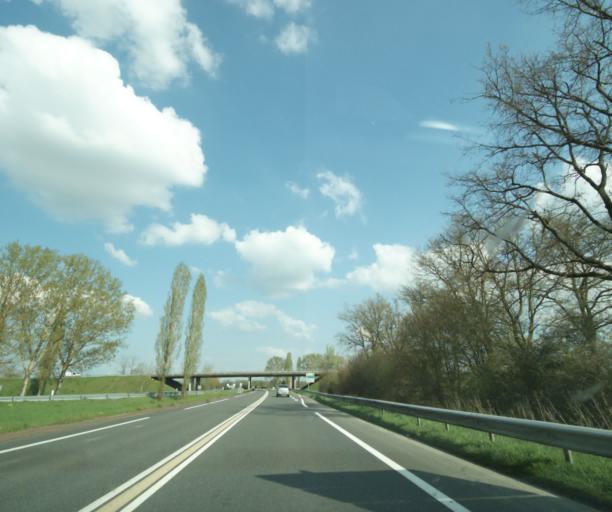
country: FR
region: Auvergne
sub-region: Departement de l'Allier
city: Bessay-sur-Allier
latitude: 46.4758
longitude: 3.3141
